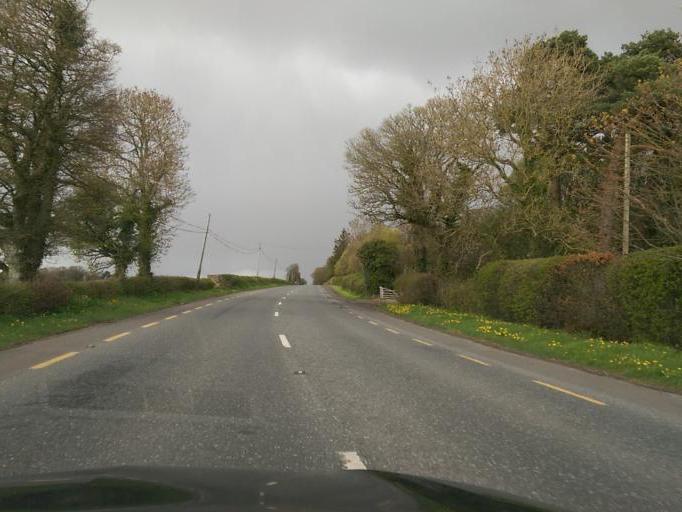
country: IE
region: Leinster
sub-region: An Mhi
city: Dunshaughlin
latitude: 53.5573
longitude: -6.5768
